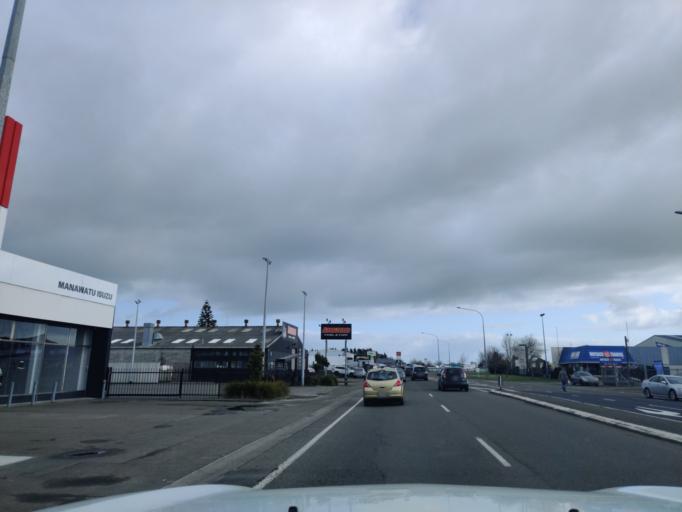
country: NZ
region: Manawatu-Wanganui
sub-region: Palmerston North City
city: Palmerston North
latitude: -40.3394
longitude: 175.5966
